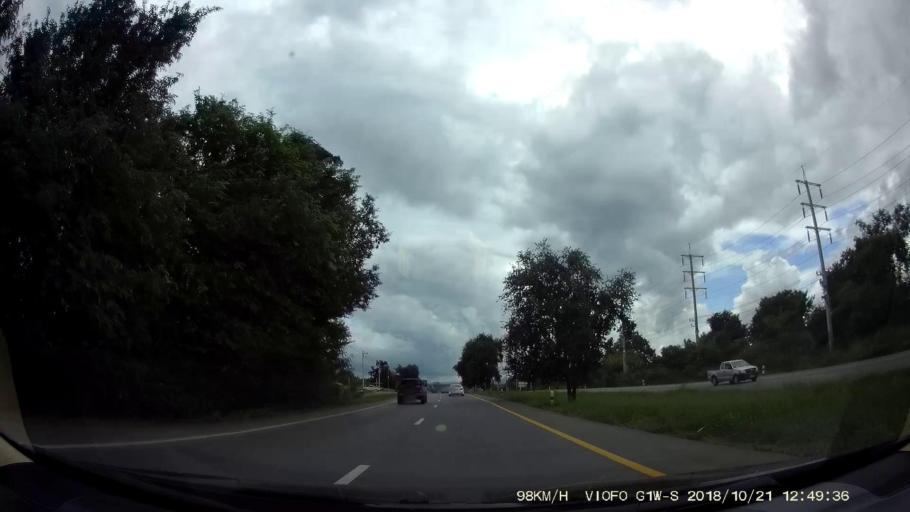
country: TH
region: Nakhon Ratchasima
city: Amphoe Sikhiu
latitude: 14.8942
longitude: 101.6851
